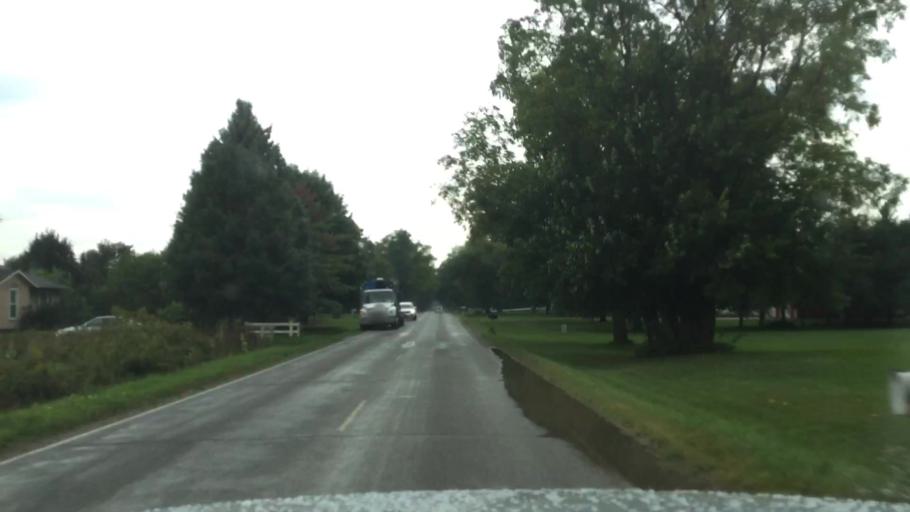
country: US
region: Michigan
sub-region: Shiawassee County
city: Perry
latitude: 42.8927
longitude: -84.2068
